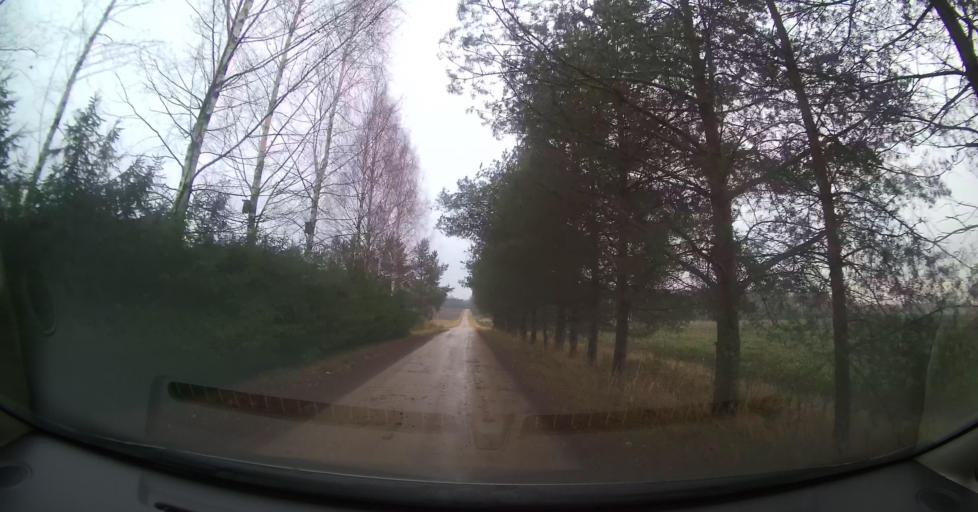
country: EE
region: Tartu
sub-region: Alatskivi vald
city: Kallaste
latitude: 58.3886
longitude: 27.0246
